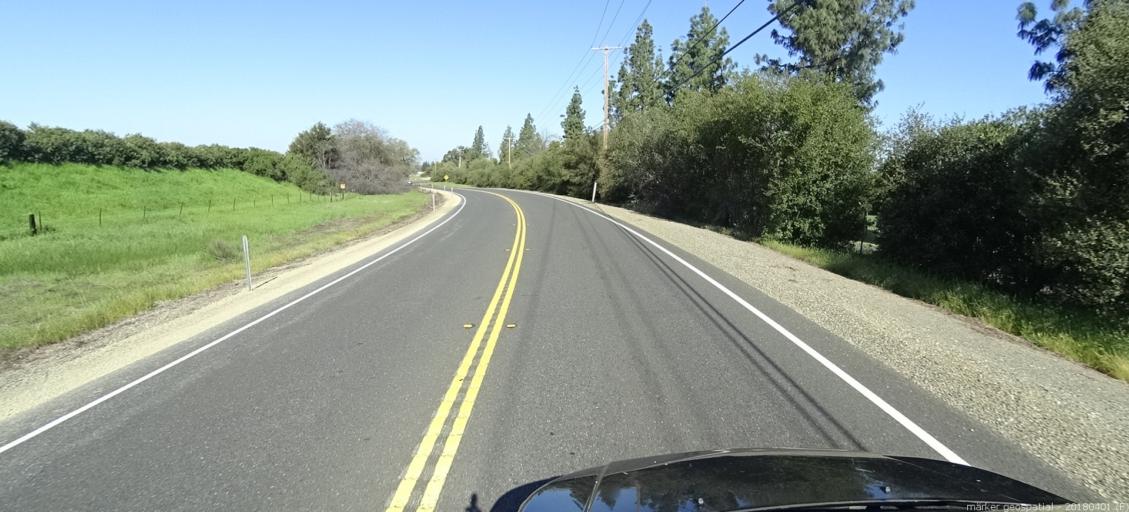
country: US
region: California
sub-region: Sacramento County
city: Rancho Murieta
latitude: 38.4899
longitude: -121.0865
